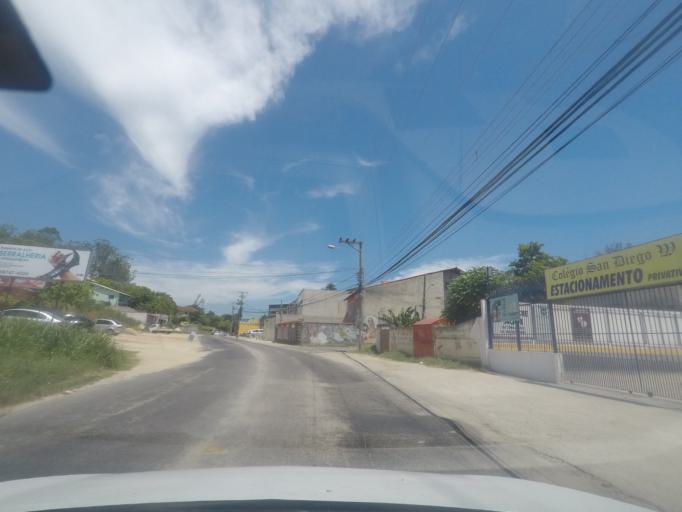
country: BR
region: Rio de Janeiro
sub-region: Itaguai
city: Itaguai
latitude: -22.9982
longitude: -43.6500
